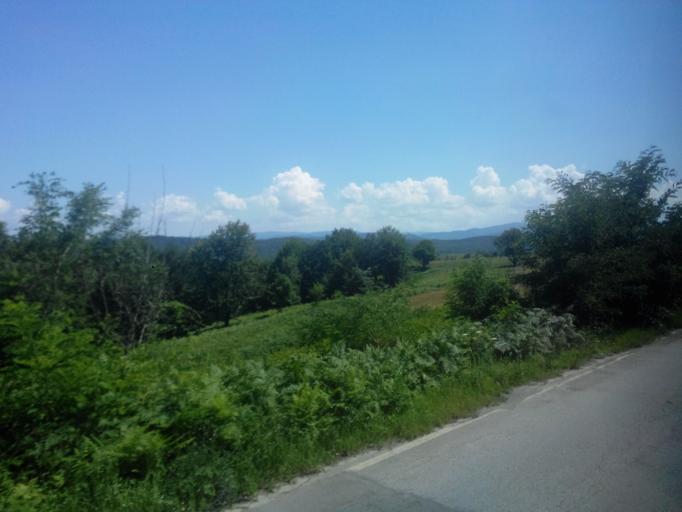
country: RO
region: Timis
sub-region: Comuna Curtea
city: Curtea
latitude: 45.8628
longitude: 22.3429
